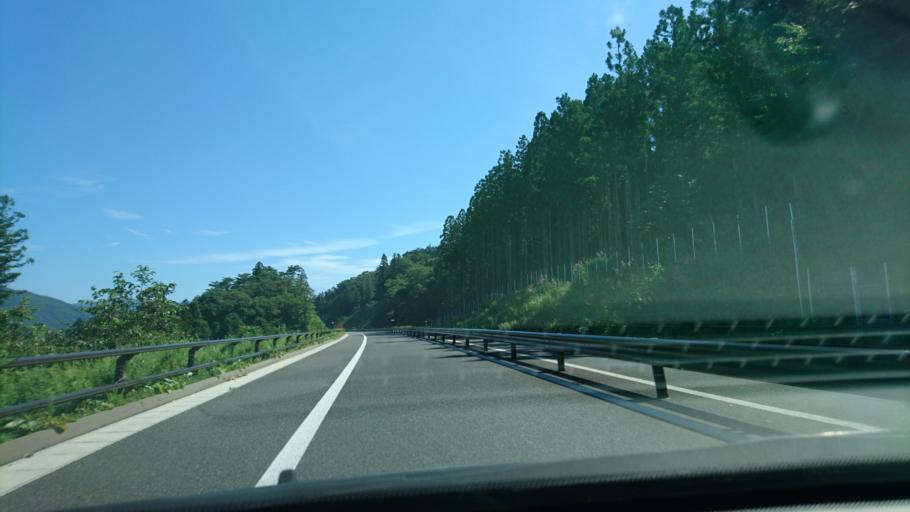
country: JP
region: Iwate
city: Tono
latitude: 39.3039
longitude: 141.4359
